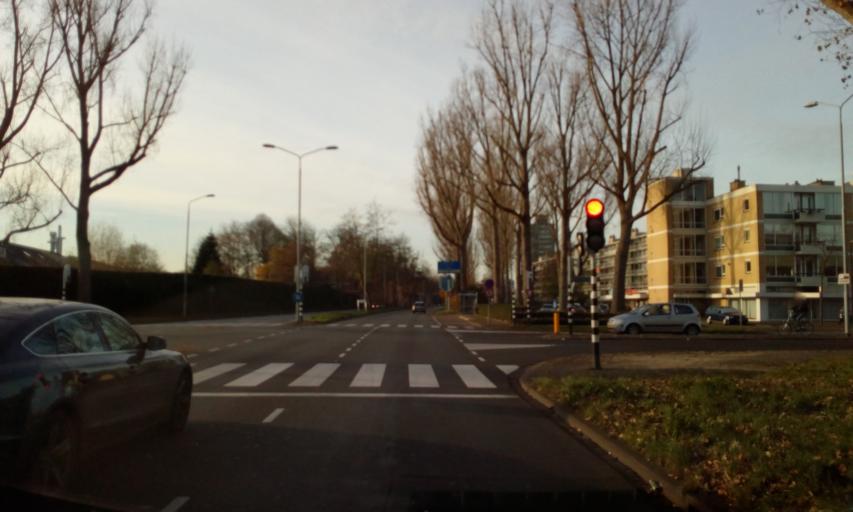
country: NL
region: South Holland
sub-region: Gemeente Leidschendam-Voorburg
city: Voorburg
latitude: 52.0903
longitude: 4.3918
